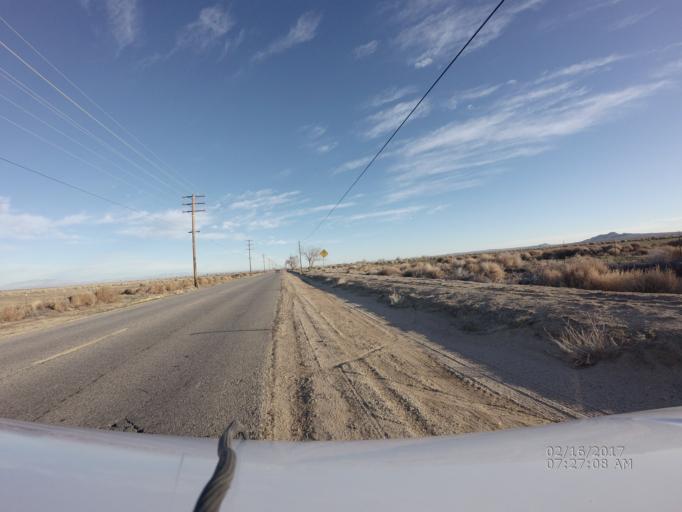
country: US
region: California
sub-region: Los Angeles County
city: Littlerock
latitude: 34.5973
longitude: -117.9694
